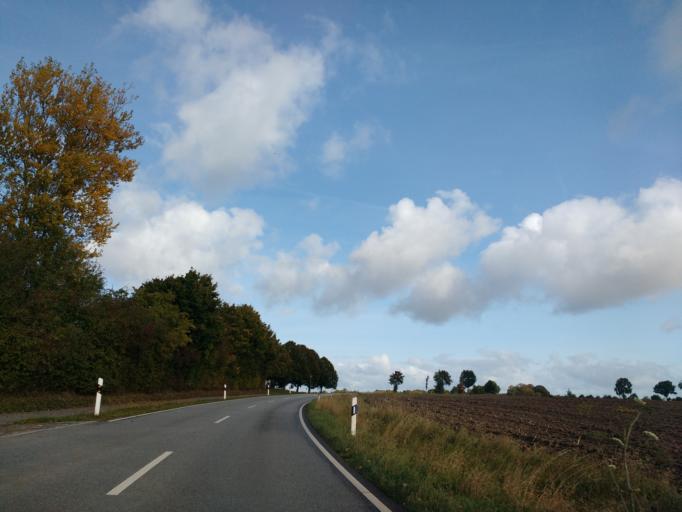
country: DE
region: Schleswig-Holstein
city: Neustadt in Holstein
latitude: 54.1197
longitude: 10.8198
